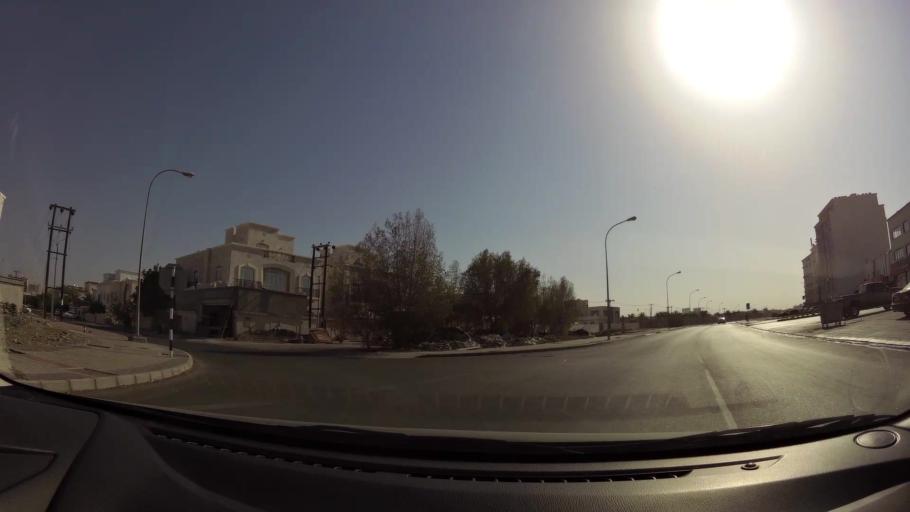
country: OM
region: Muhafazat Masqat
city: As Sib al Jadidah
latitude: 23.6211
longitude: 58.2022
